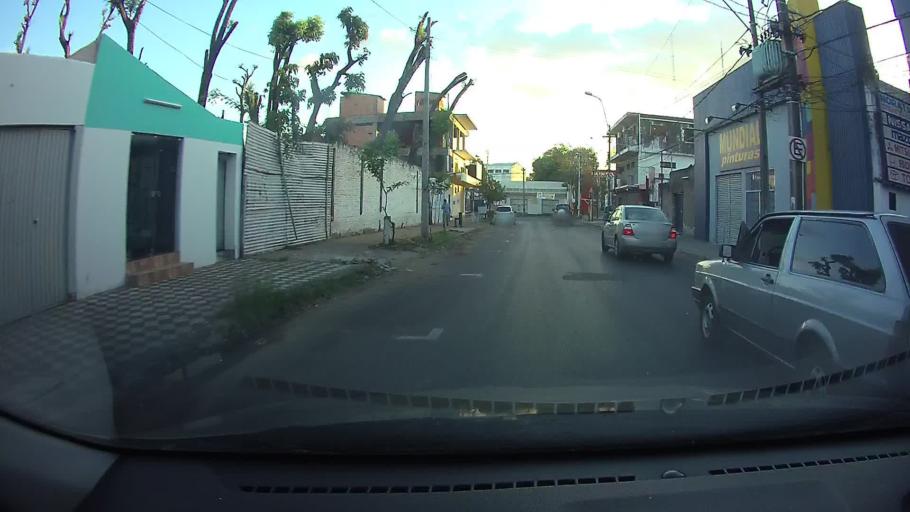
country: PY
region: Central
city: Lambare
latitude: -25.3135
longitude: -57.5802
